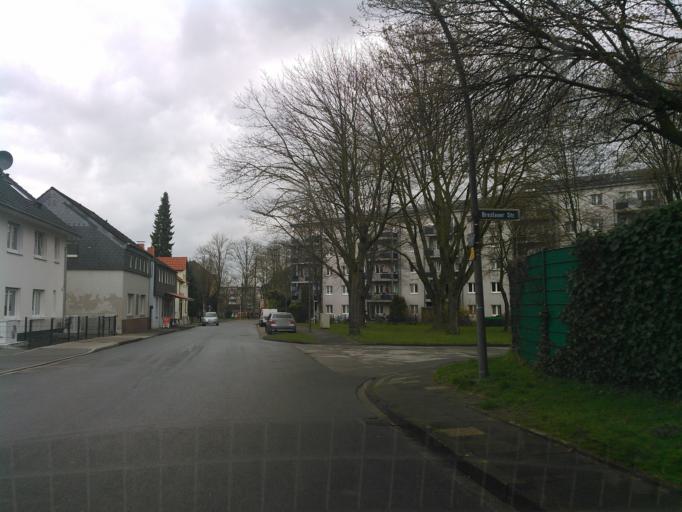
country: DE
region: North Rhine-Westphalia
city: Marl
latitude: 51.6508
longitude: 7.0930
